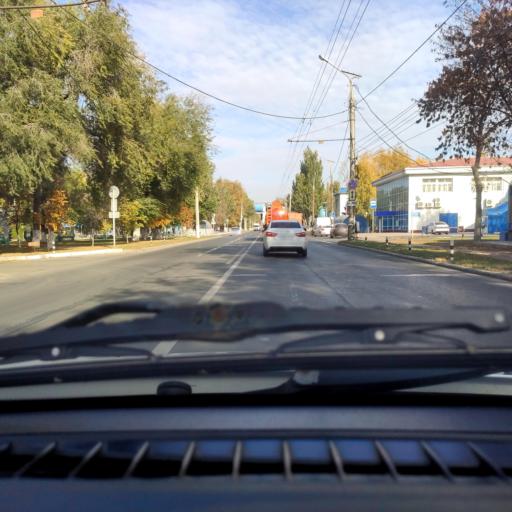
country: RU
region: Samara
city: Tol'yatti
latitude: 53.5546
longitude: 49.4508
